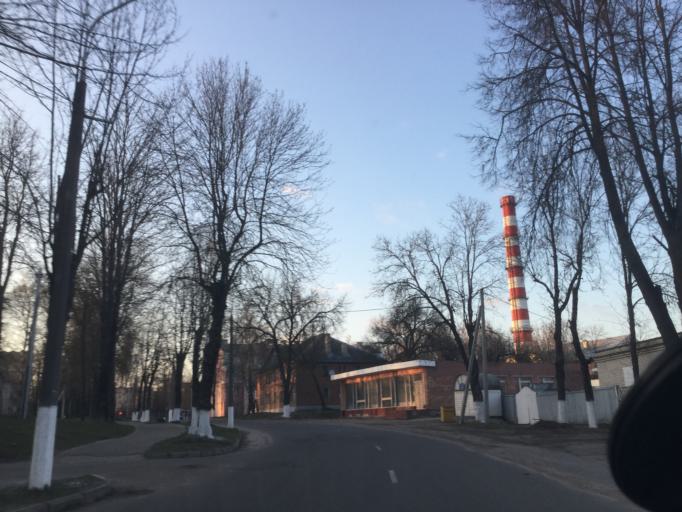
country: BY
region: Vitebsk
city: Vitebsk
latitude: 55.1651
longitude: 30.1309
